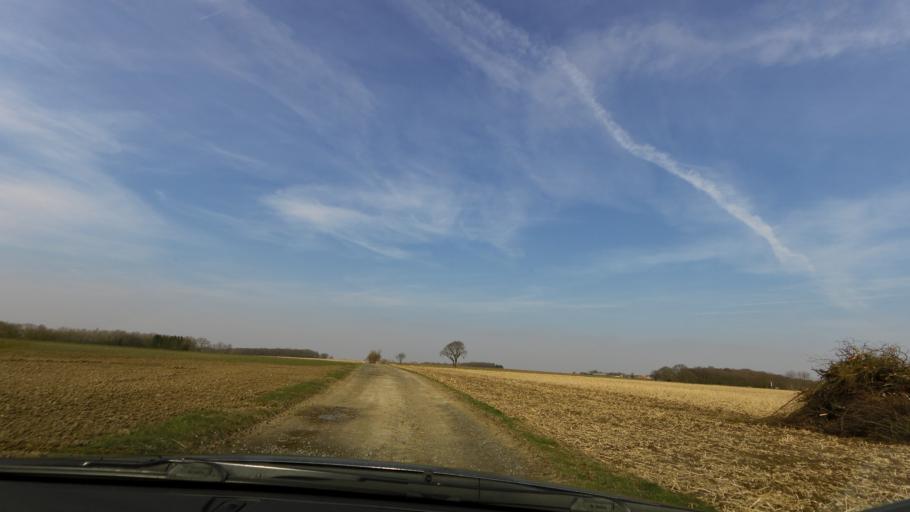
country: NL
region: Limburg
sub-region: Valkenburg aan de Geul
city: Schin op Geul
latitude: 50.8223
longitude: 5.8646
